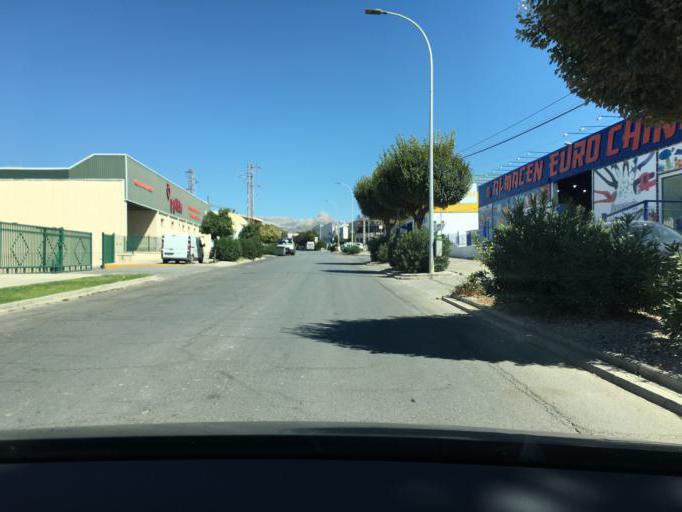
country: ES
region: Andalusia
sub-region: Provincia de Granada
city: Albolote
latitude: 37.2279
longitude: -3.6487
